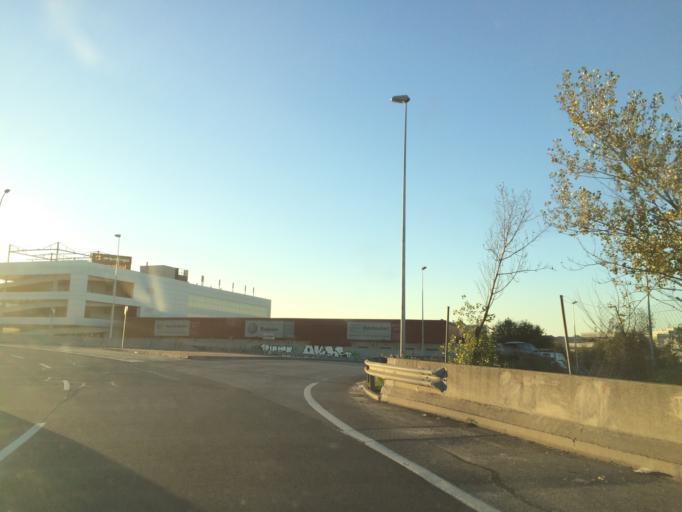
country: ES
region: Madrid
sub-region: Provincia de Madrid
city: Alcobendas
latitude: 40.5333
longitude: -3.6395
